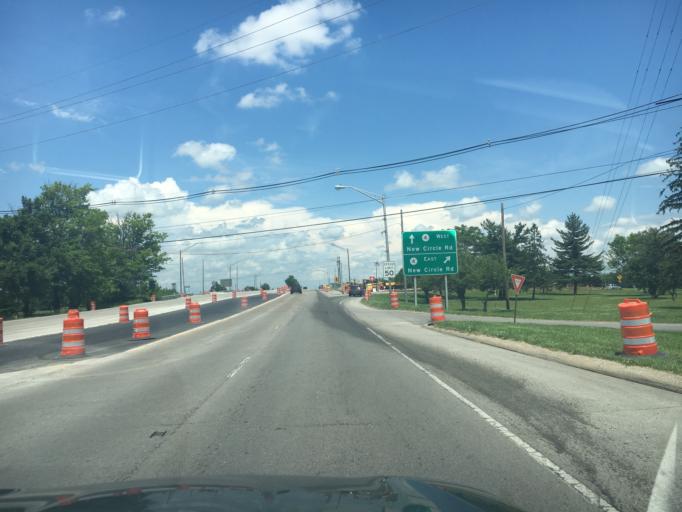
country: US
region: Kentucky
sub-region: Fayette County
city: Lexington-Fayette
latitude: 38.0719
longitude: -84.4962
